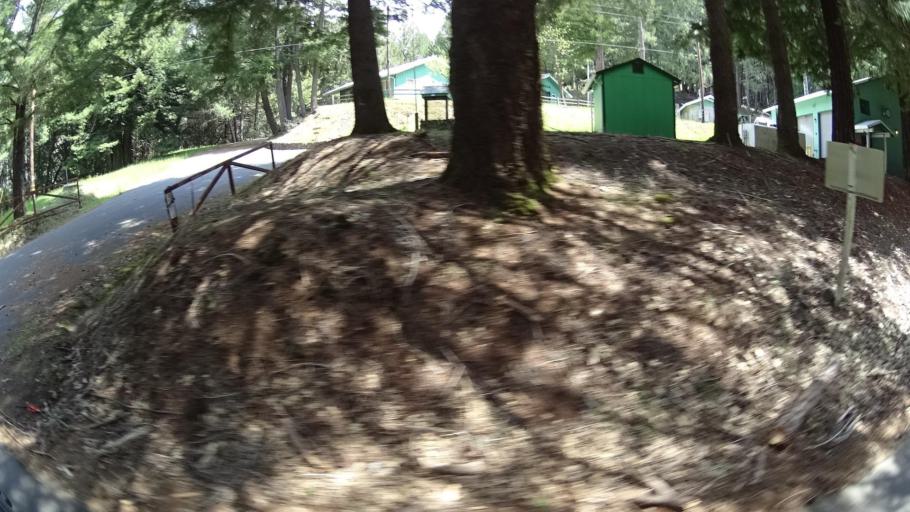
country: US
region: California
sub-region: Humboldt County
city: Redway
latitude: 40.0563
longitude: -123.9622
